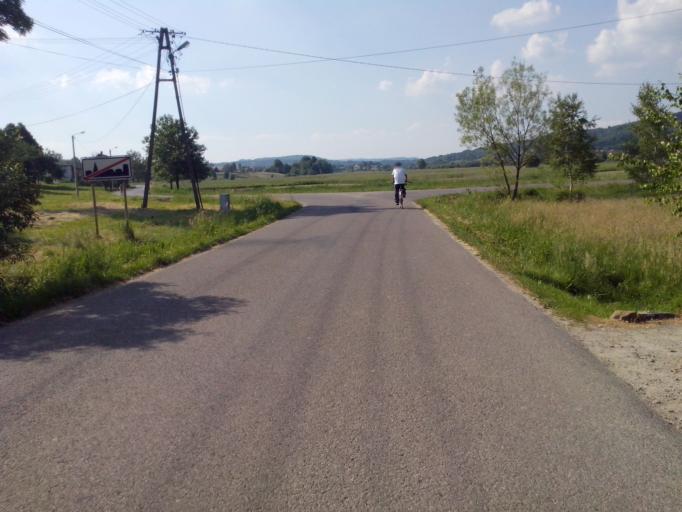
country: PL
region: Subcarpathian Voivodeship
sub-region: Powiat brzozowski
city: Blizne
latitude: 49.7494
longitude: 21.9696
